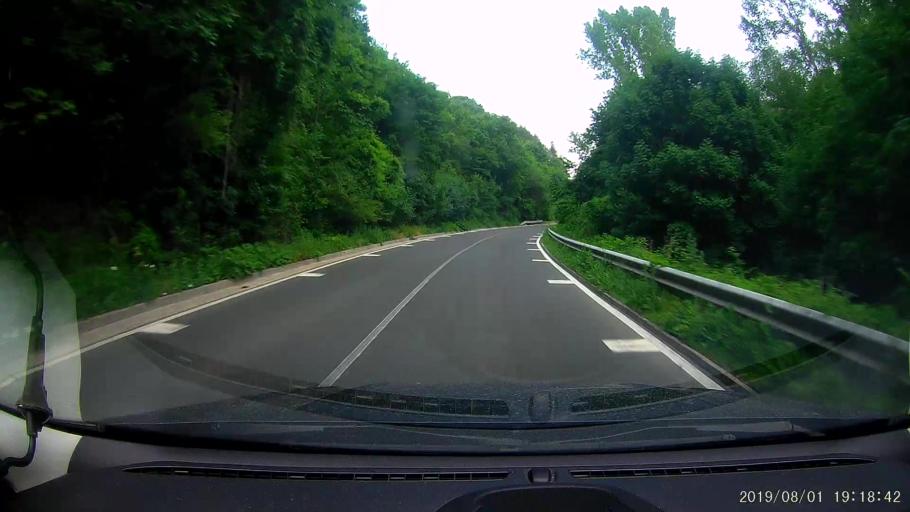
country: BG
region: Shumen
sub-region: Obshtina Smyadovo
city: Smyadovo
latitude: 42.9093
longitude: 26.9401
